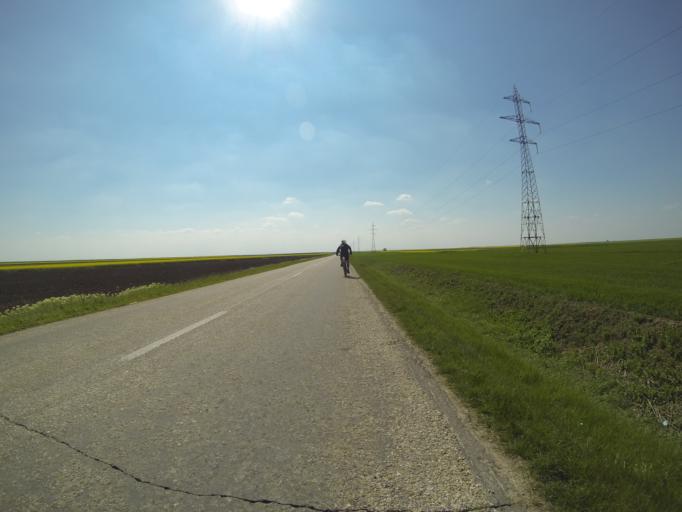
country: RO
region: Dolj
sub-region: Comuna Unirea
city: Unirea
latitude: 44.1633
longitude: 23.1543
